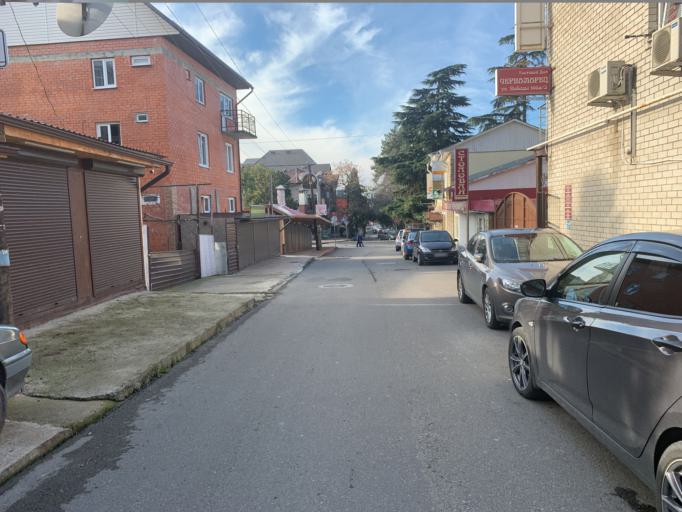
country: RU
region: Krasnodarskiy
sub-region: Sochi City
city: Lazarevskoye
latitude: 43.9206
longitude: 39.3193
